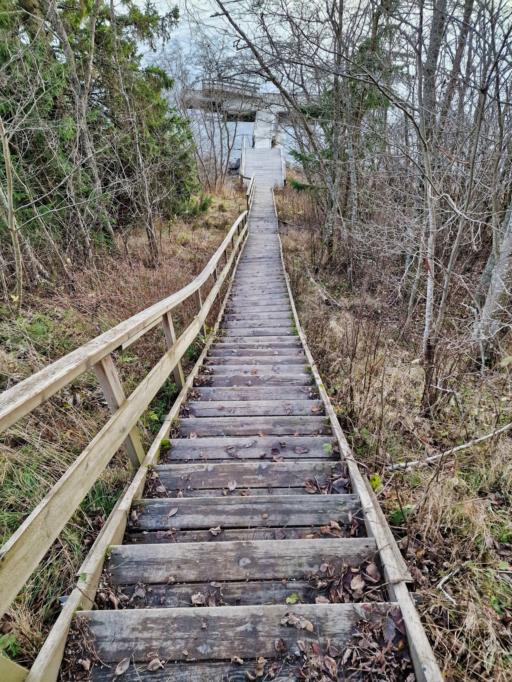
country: NO
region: Akershus
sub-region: Nes
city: Arnes
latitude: 60.1470
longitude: 11.4587
